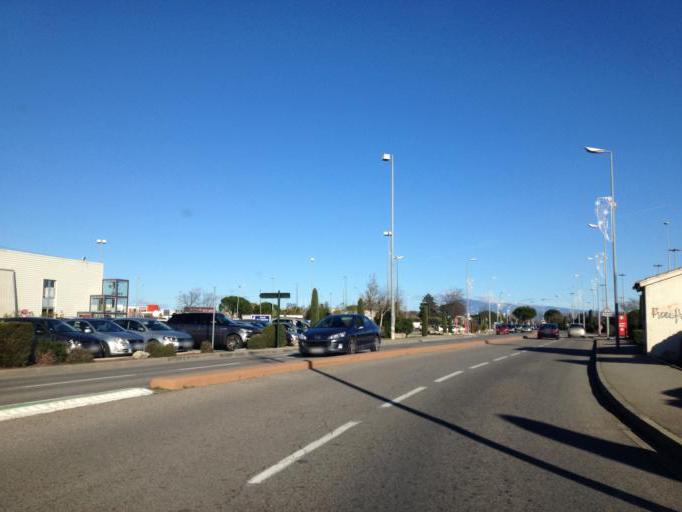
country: FR
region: Provence-Alpes-Cote d'Azur
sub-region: Departement du Vaucluse
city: Vedene
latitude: 43.9833
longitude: 4.8778
